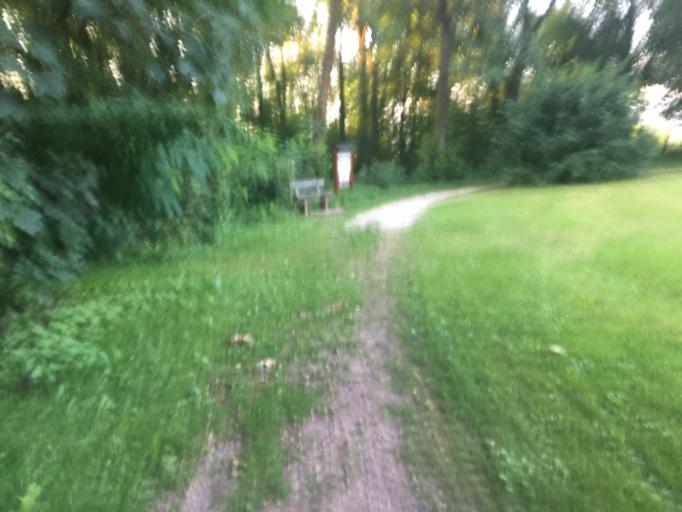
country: DE
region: Hesse
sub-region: Regierungsbezirk Darmstadt
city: Gelnhausen
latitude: 50.1839
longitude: 9.1486
